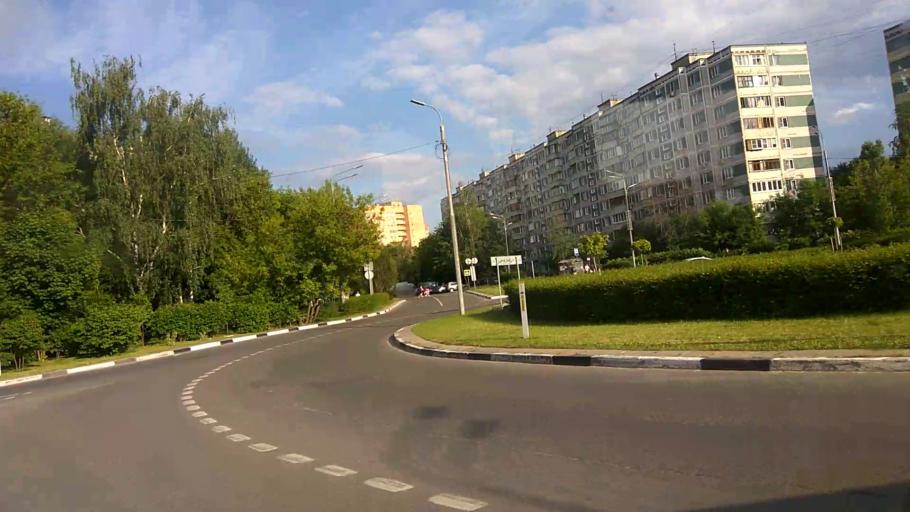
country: RU
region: Moskovskaya
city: Mytishchi
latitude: 55.9061
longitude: 37.7083
